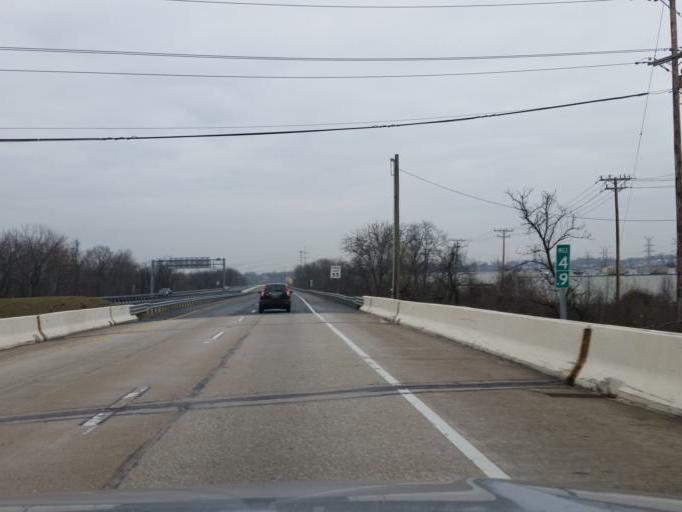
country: US
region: Maryland
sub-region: Baltimore County
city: Baltimore Highlands
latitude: 39.2306
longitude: -76.6418
